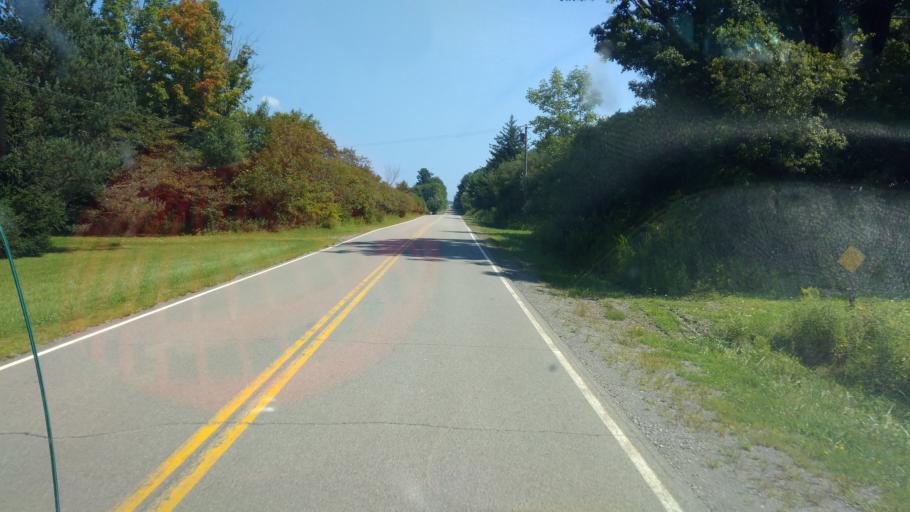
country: US
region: New York
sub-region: Allegany County
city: Alfred
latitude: 42.2941
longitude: -77.9119
